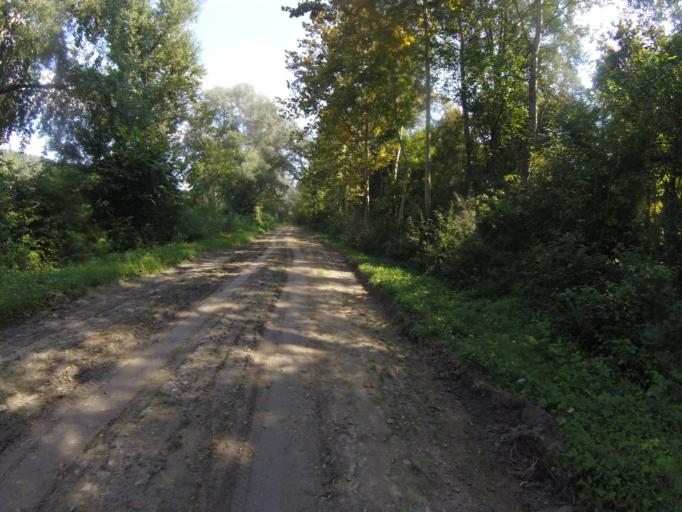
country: HU
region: Bacs-Kiskun
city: Baja
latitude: 46.1991
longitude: 18.8993
